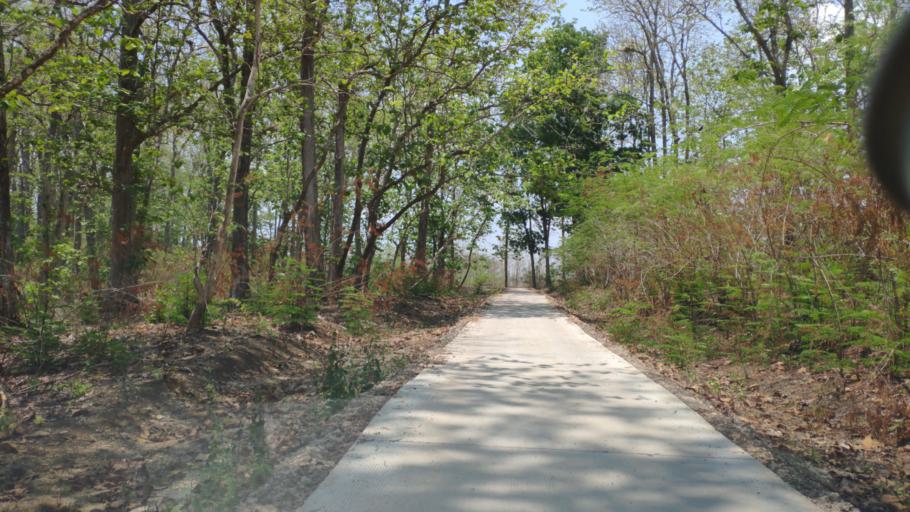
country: ID
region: Central Java
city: Botoh
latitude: -7.0742
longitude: 111.4821
